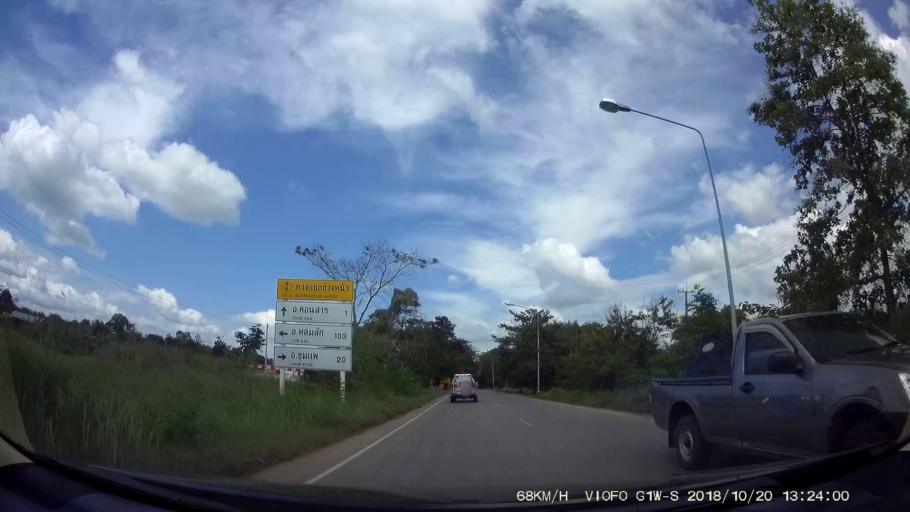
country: TH
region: Chaiyaphum
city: Khon San
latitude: 16.5897
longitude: 101.9245
